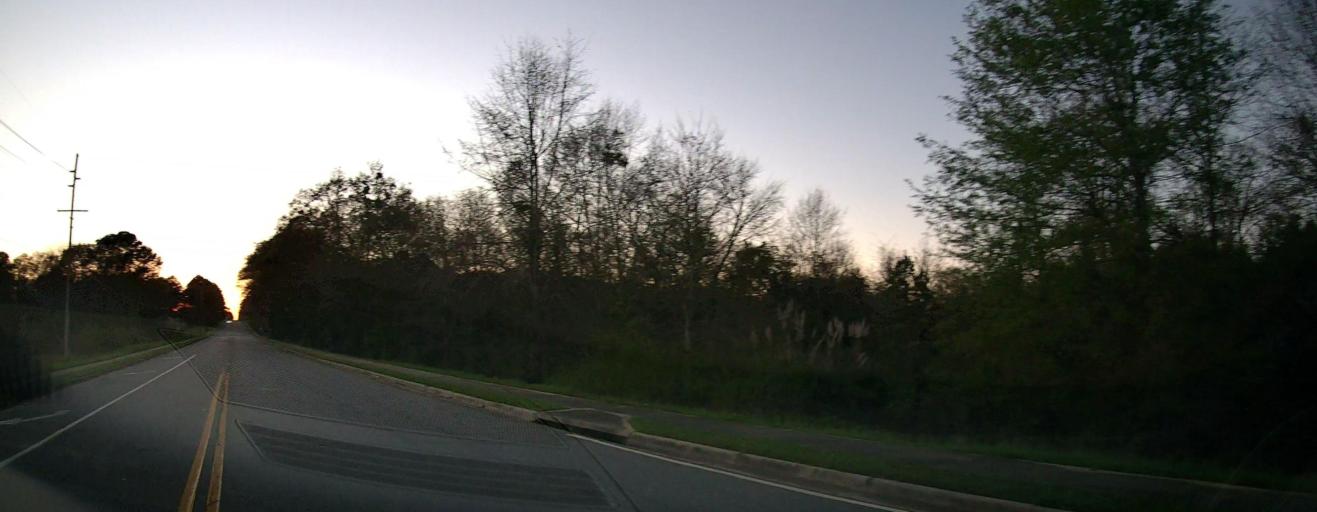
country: US
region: Georgia
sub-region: Crisp County
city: Cordele
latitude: 31.9547
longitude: -83.7536
